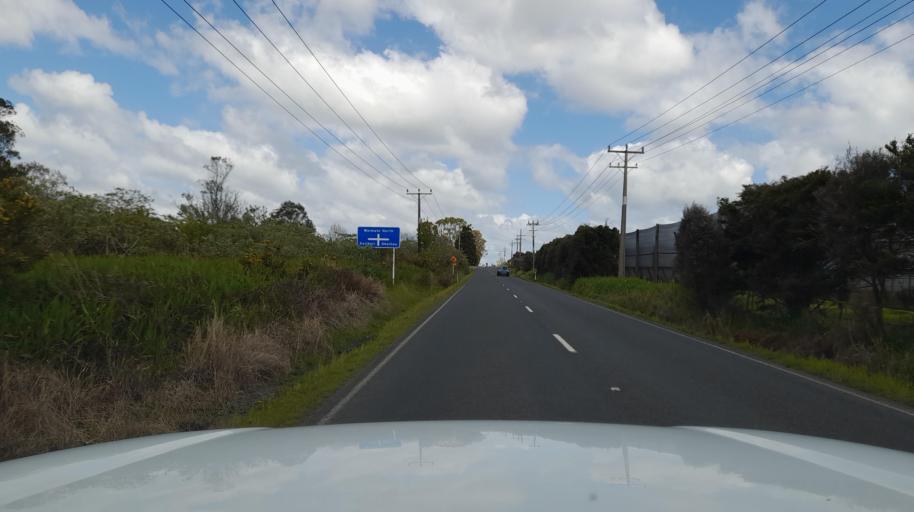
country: NZ
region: Northland
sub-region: Far North District
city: Kerikeri
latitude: -35.2632
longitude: 173.9038
